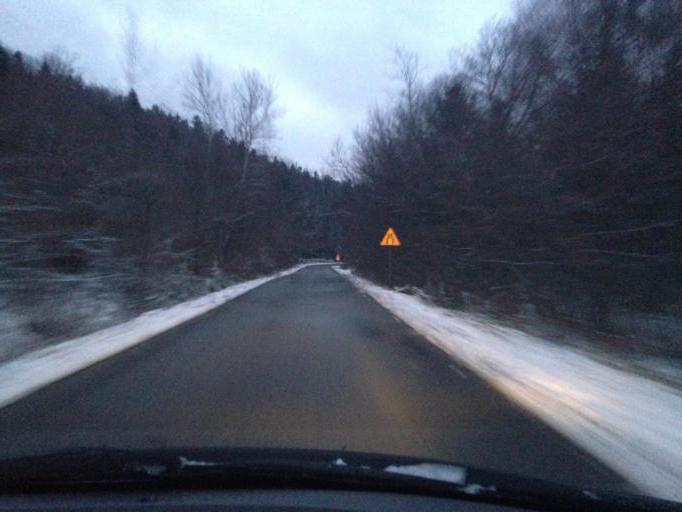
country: PL
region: Subcarpathian Voivodeship
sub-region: Powiat jasielski
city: Krempna
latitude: 49.5144
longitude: 21.5420
